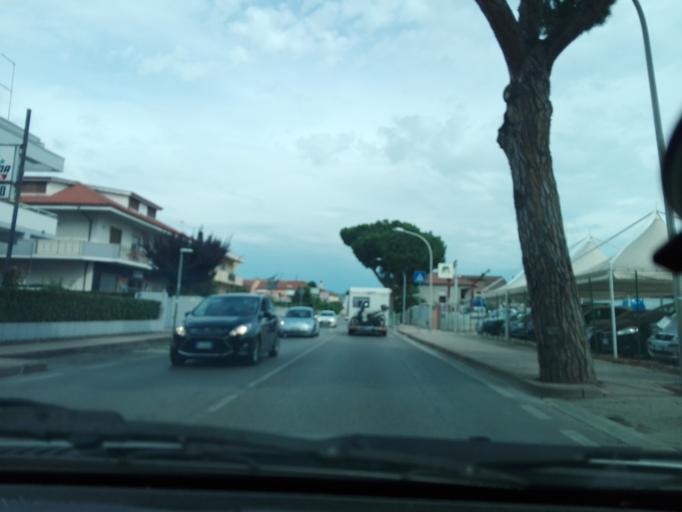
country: IT
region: Abruzzo
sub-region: Provincia di Pescara
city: San Martino Bassa
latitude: 42.5248
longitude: 14.1399
